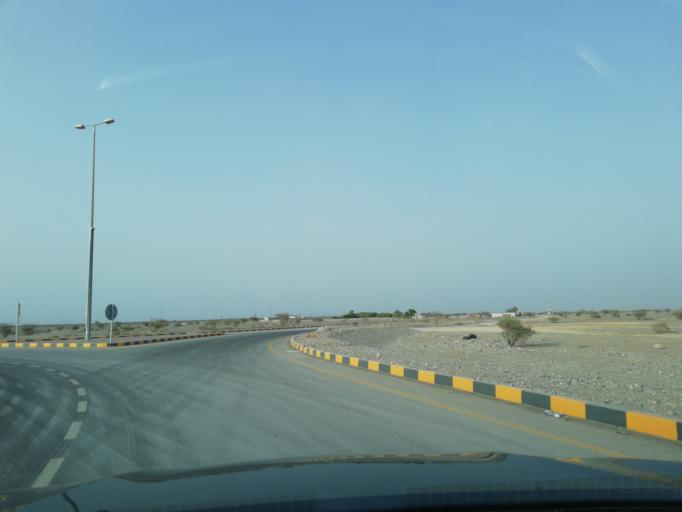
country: OM
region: Al Batinah
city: Barka'
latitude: 23.6136
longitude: 57.9099
